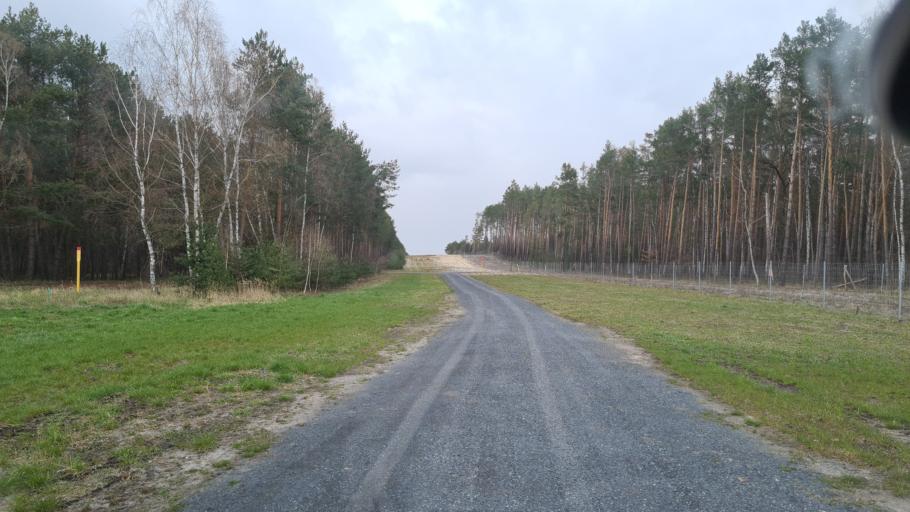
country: DE
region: Brandenburg
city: Finsterwalde
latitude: 51.5626
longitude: 13.6829
